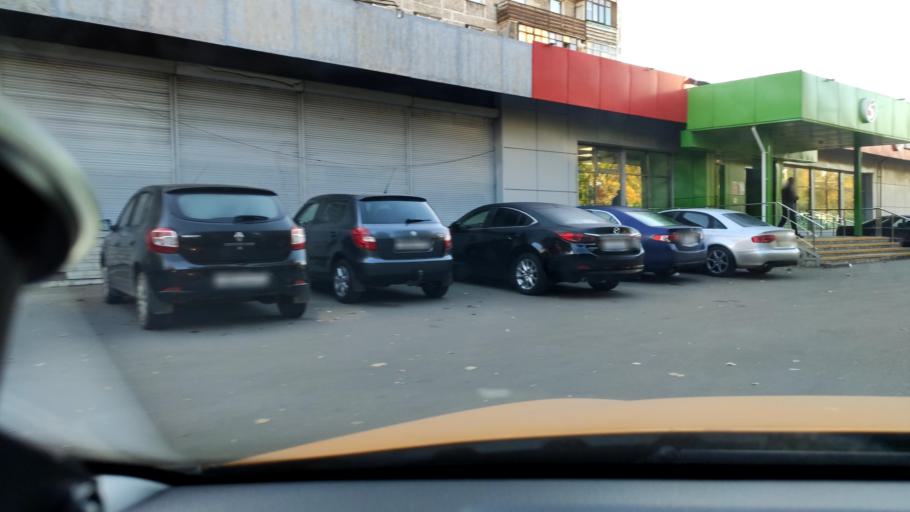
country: RU
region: Moscow
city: Vykhino-Zhulebino
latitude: 55.6936
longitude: 37.8229
